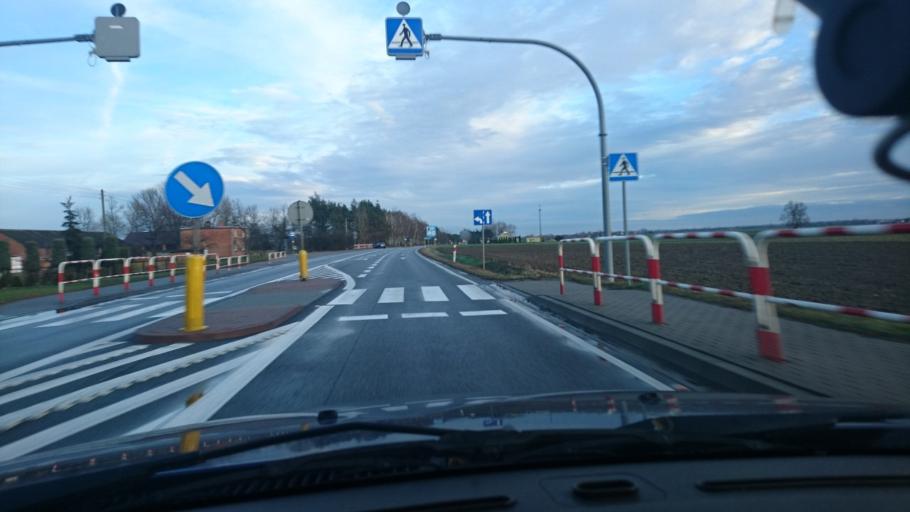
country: PL
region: Greater Poland Voivodeship
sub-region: Powiat kepinski
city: Leka Opatowska
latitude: 51.2244
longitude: 18.1073
